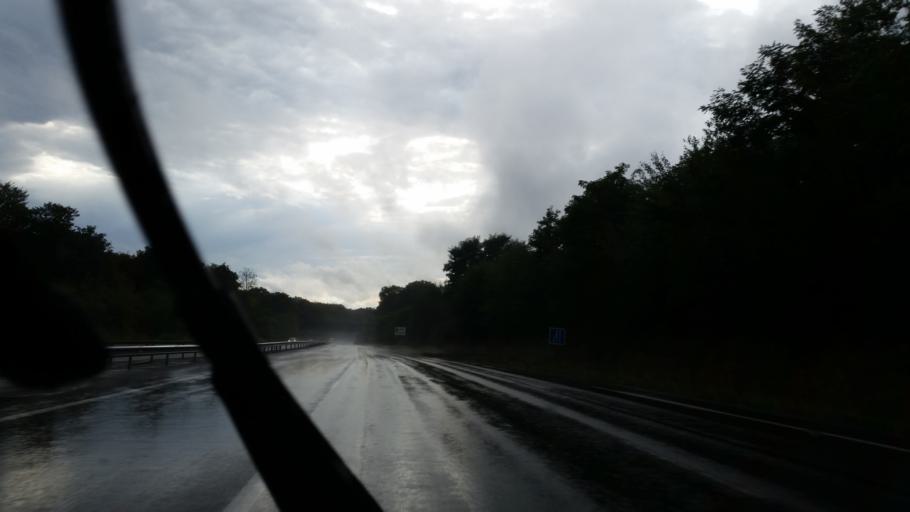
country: FR
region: Franche-Comte
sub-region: Departement de la Haute-Saone
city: Ronchamp
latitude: 47.6420
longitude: 6.6075
